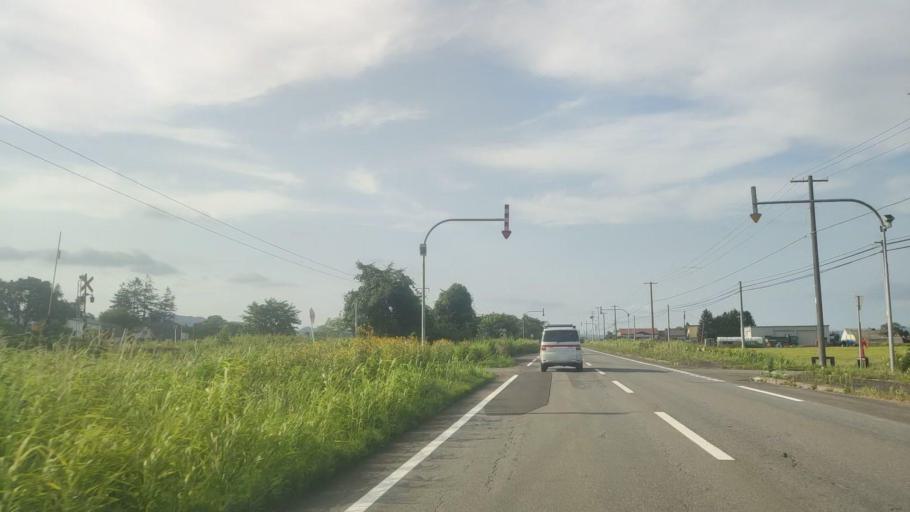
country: JP
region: Hokkaido
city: Chitose
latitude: 42.9570
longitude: 141.7985
